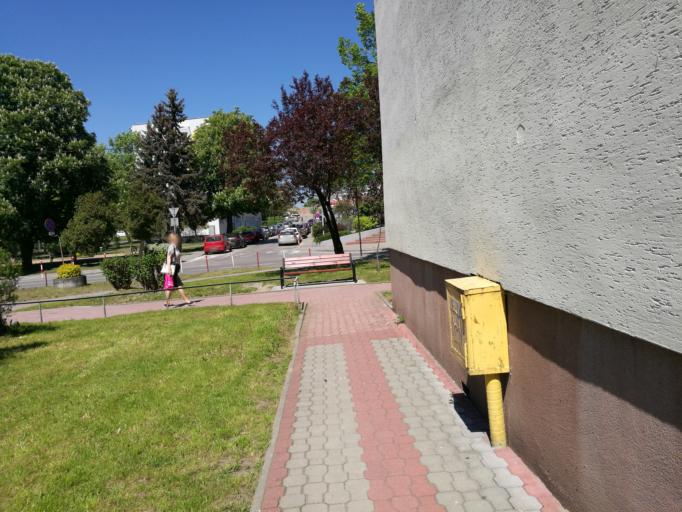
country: PL
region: Swietokrzyskie
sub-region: Powiat kielecki
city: Kielce
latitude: 50.8656
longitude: 20.6465
